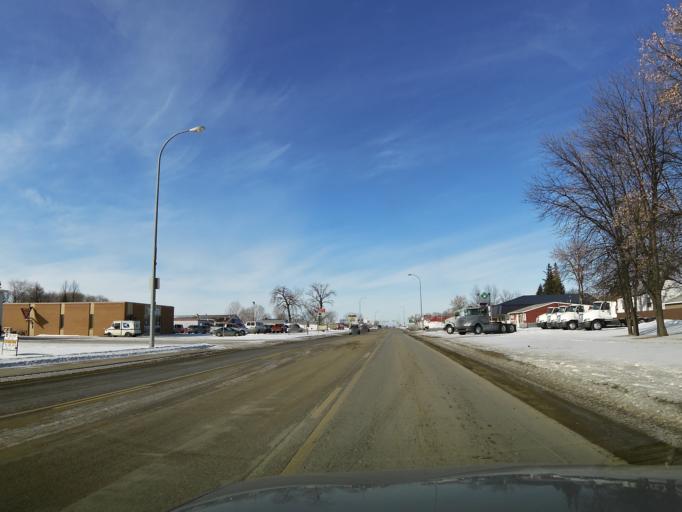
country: US
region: North Dakota
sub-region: Walsh County
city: Grafton
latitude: 48.4126
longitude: -97.4188
